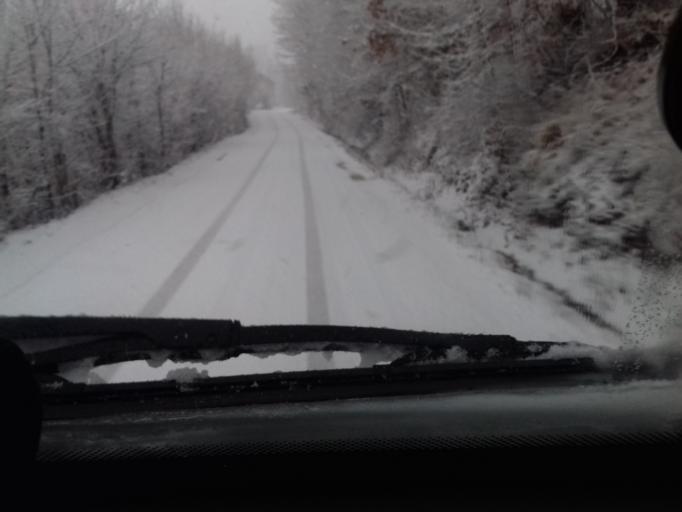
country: BA
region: Federation of Bosnia and Herzegovina
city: Lokvine
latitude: 44.2408
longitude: 17.8124
